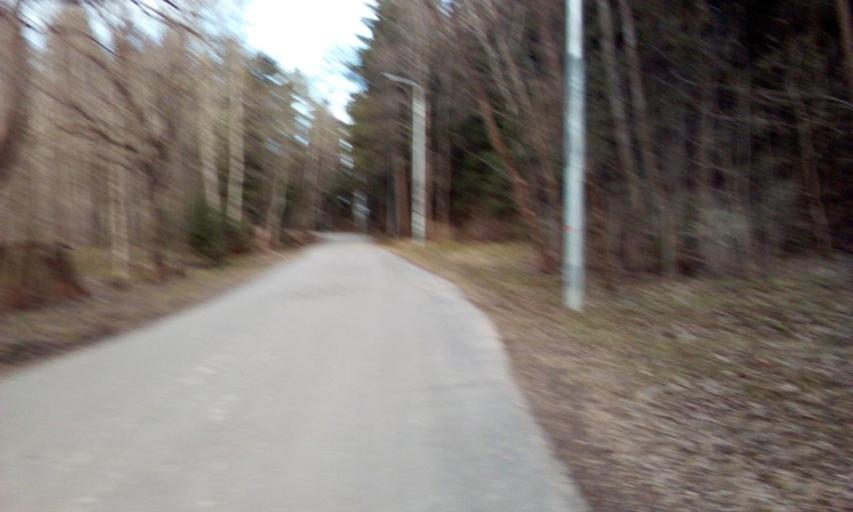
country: RU
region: Moskovskaya
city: Annino
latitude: 55.5551
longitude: 37.2293
